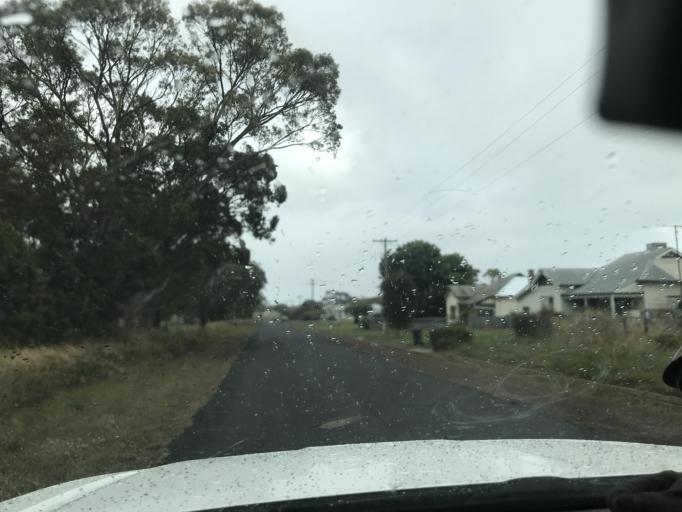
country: AU
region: Victoria
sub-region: Horsham
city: Horsham
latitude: -36.7218
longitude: 141.4753
